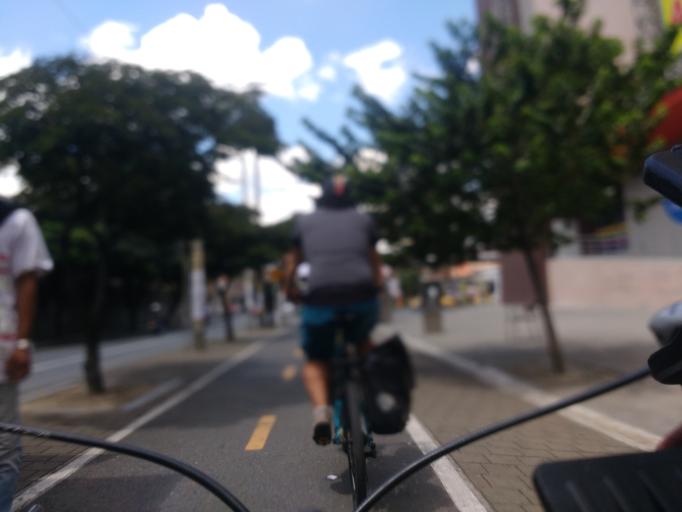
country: CO
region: Antioquia
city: Medellin
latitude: 6.2638
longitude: -75.5666
